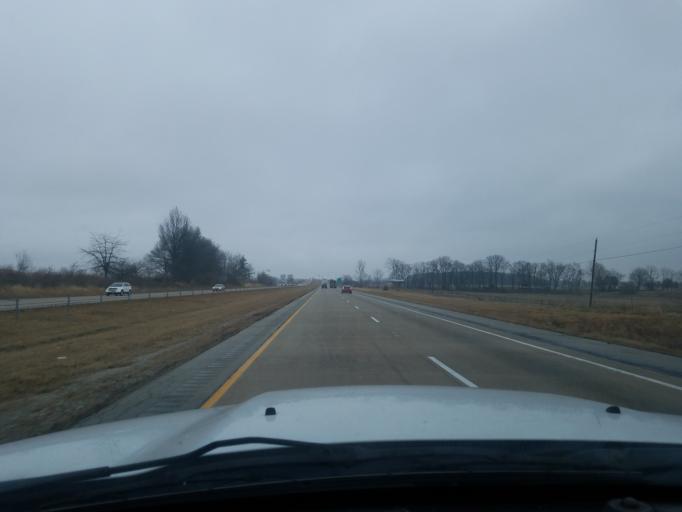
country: US
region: Indiana
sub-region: Grant County
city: Upland
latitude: 40.4632
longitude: -85.5511
